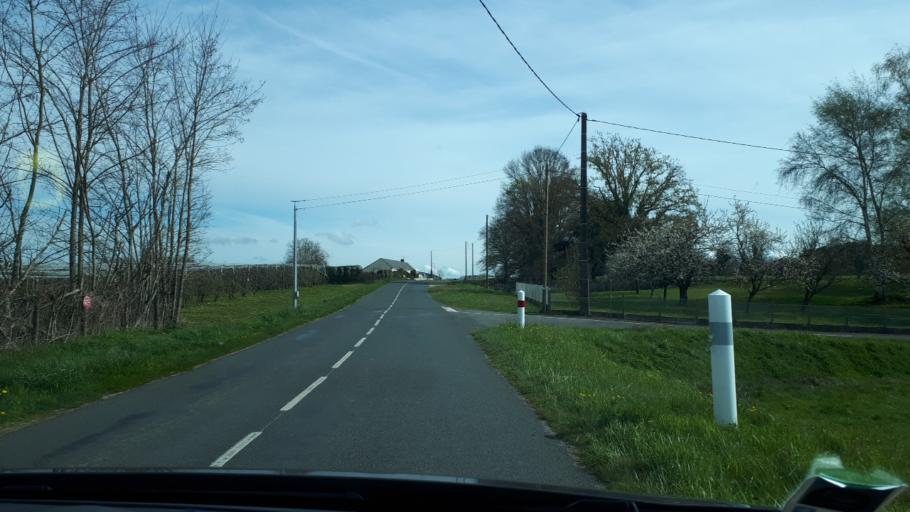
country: FR
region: Pays de la Loire
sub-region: Departement de la Sarthe
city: Yvre-le-Polin
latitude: 47.8128
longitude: 0.1239
